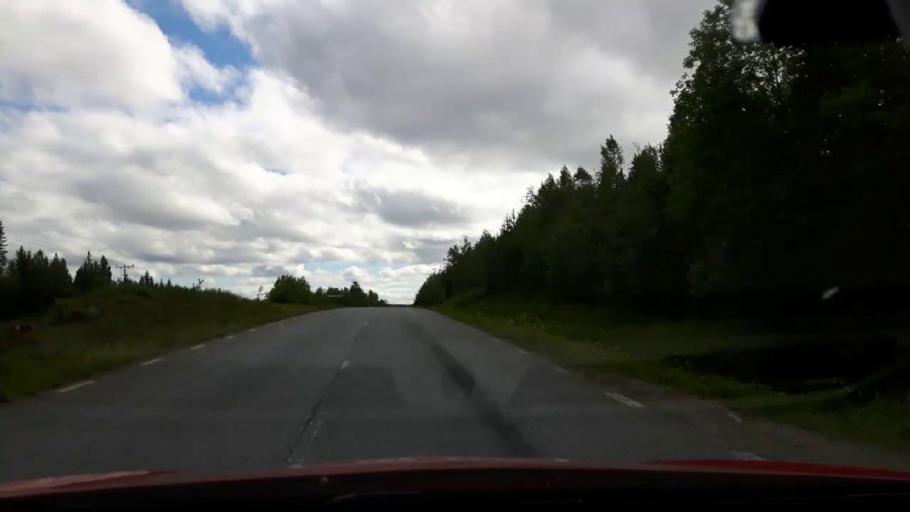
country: SE
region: Jaemtland
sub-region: Ragunda Kommun
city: Hammarstrand
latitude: 62.9733
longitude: 16.0668
